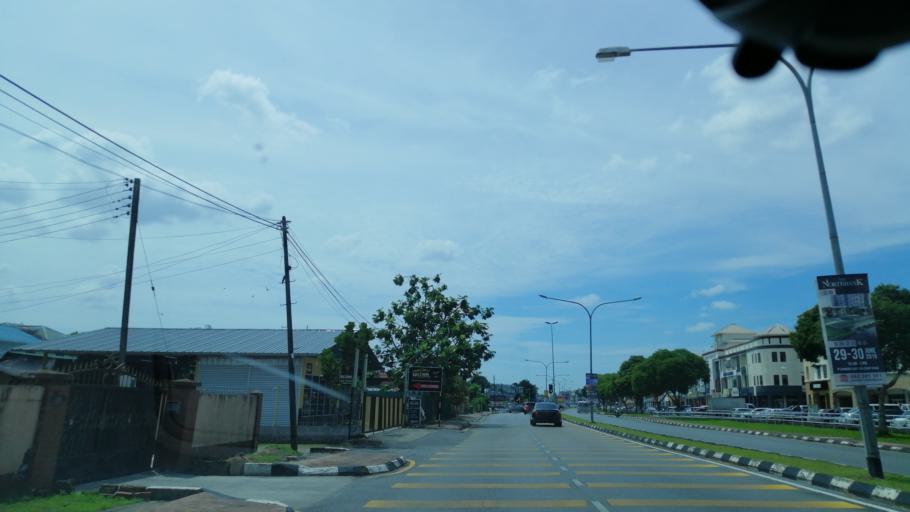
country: MY
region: Sarawak
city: Kuching
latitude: 1.5437
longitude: 110.3582
